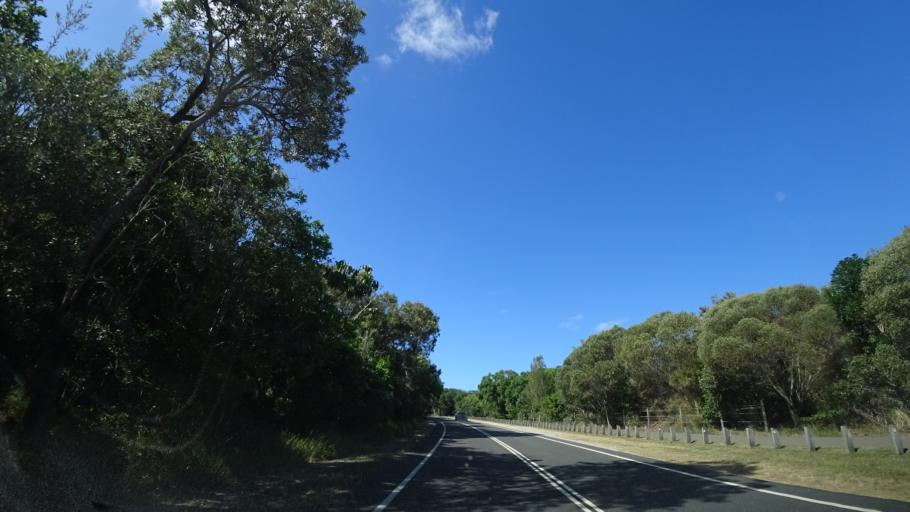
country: AU
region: Queensland
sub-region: Sunshine Coast
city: Mooloolaba
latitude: -26.6280
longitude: 153.0999
